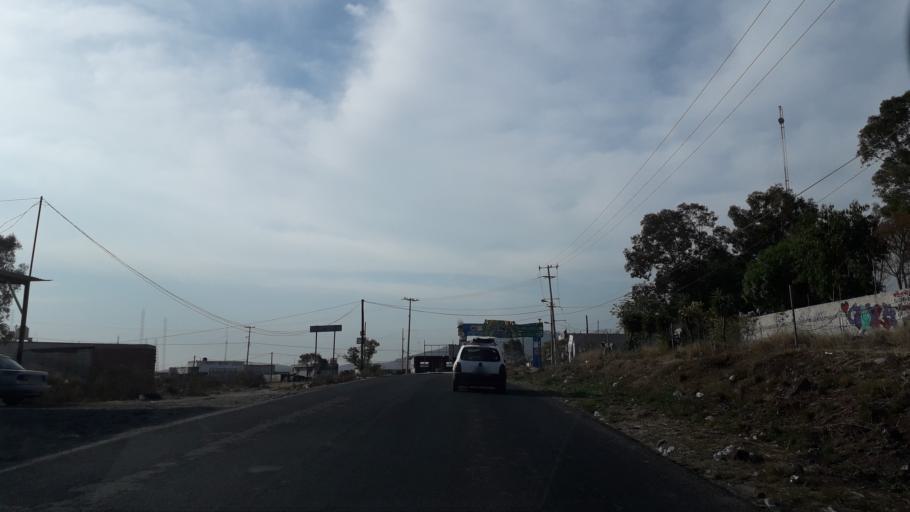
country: MX
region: Puebla
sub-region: Puebla
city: San Andres Azumiatla
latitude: 18.9114
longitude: -98.2418
